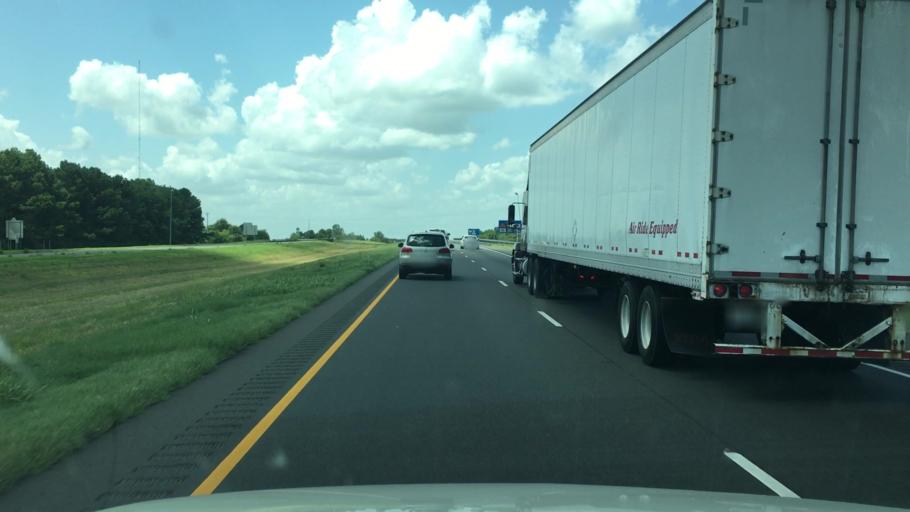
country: US
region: Arkansas
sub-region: Hempstead County
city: Hope
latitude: 33.6926
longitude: -93.5963
